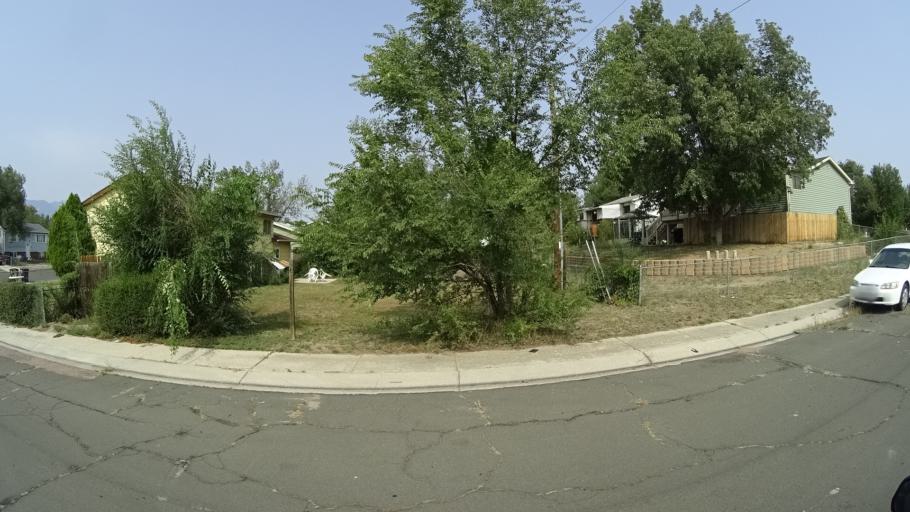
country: US
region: Colorado
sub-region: El Paso County
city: Stratmoor
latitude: 38.7953
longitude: -104.7638
